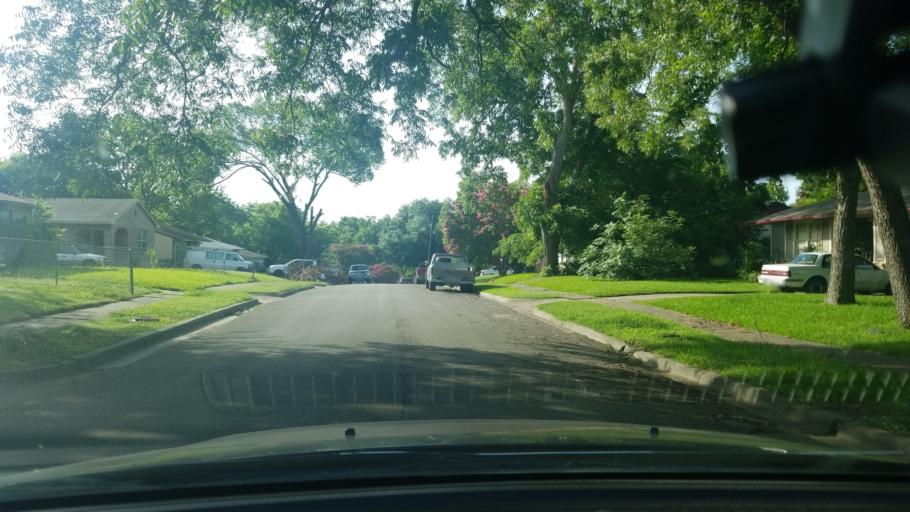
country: US
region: Texas
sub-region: Dallas County
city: Highland Park
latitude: 32.7994
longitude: -96.7143
